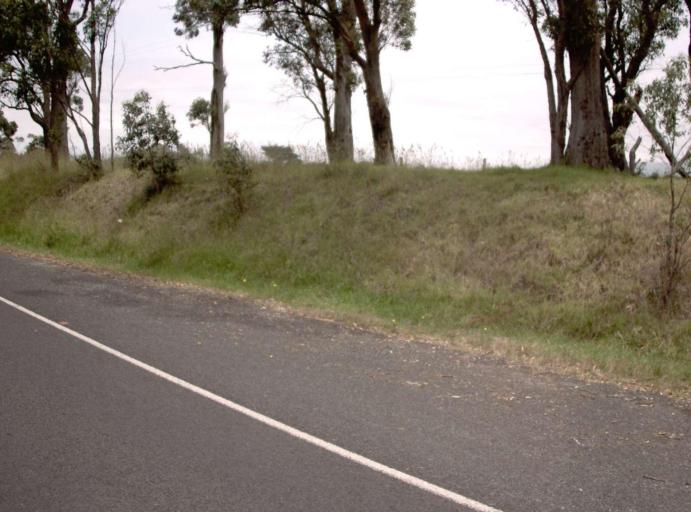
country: AU
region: Victoria
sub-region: Latrobe
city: Traralgon
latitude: -38.4742
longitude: 146.7168
